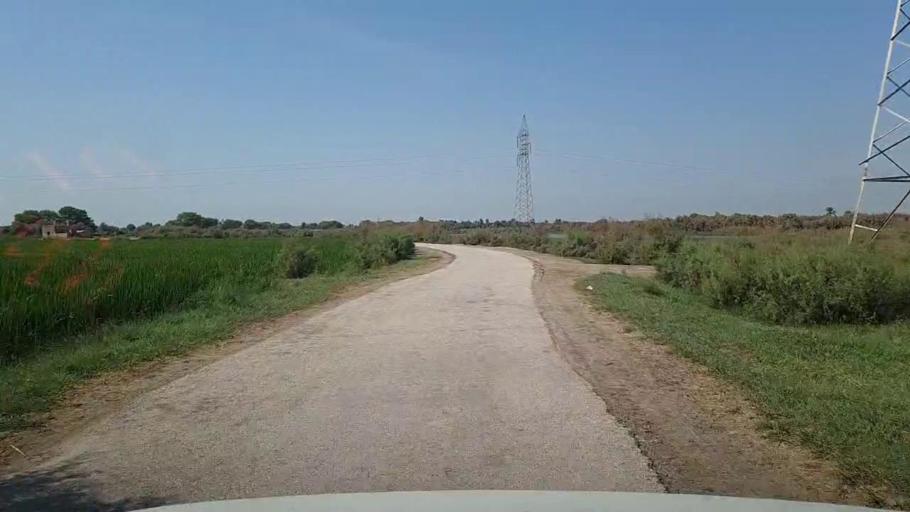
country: PK
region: Sindh
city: Kandhkot
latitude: 28.3345
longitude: 69.3659
